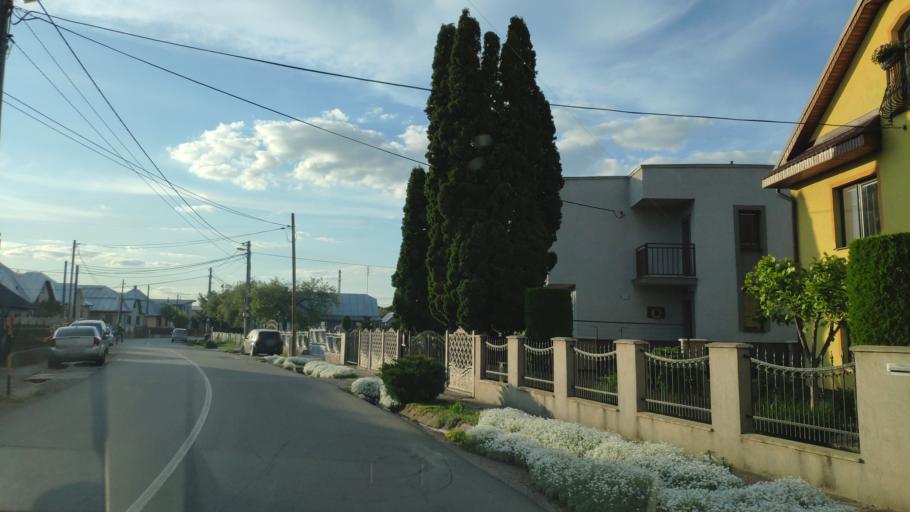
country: SK
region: Kosicky
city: Kosice
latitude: 48.6485
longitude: 21.3208
